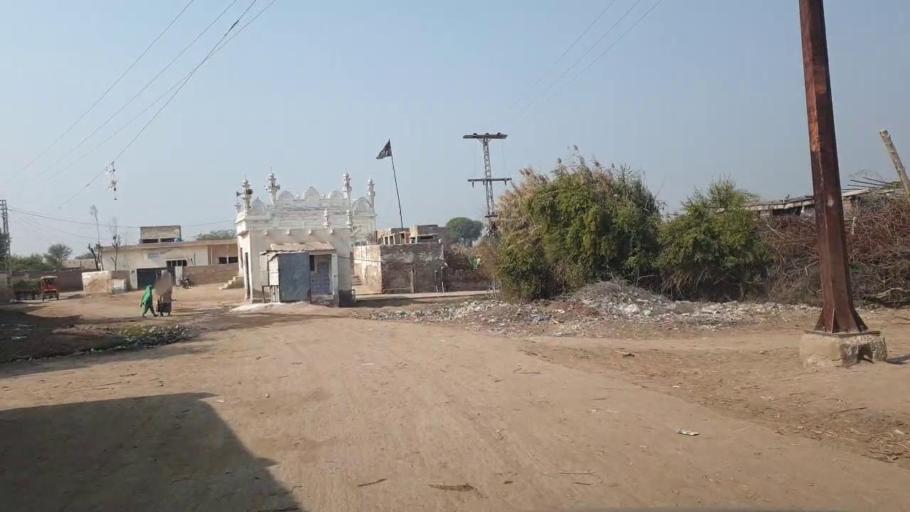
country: PK
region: Sindh
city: Hala
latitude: 25.9498
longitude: 68.4679
